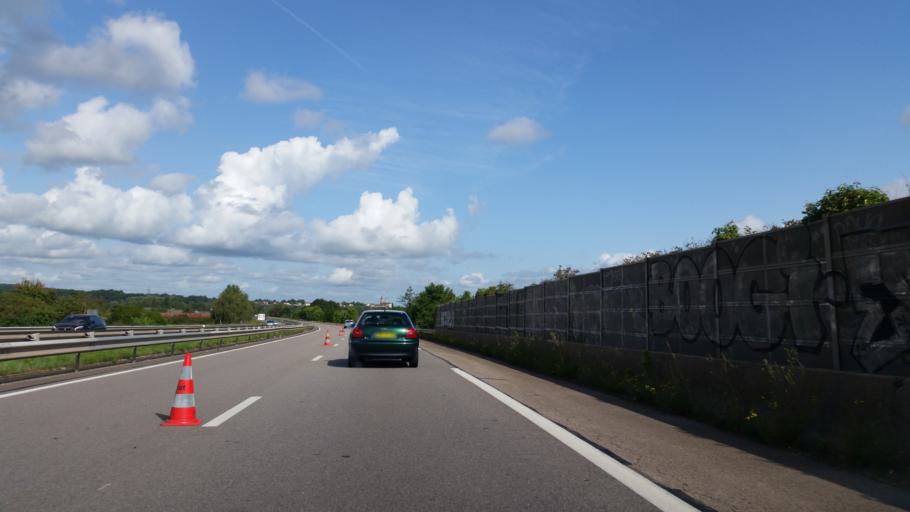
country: FR
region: Lorraine
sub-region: Departement des Vosges
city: Dogneville
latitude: 48.2194
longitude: 6.4528
